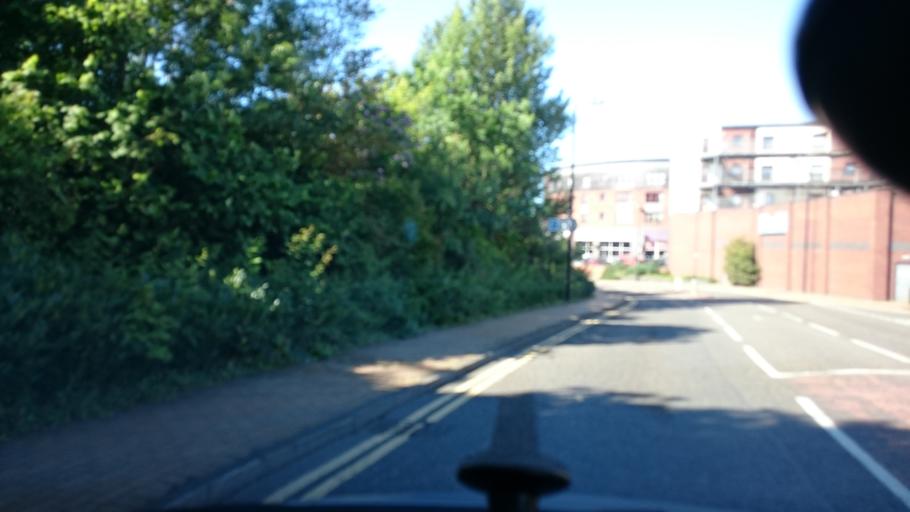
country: GB
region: Scotland
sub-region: Clackmannanshire
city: Alloa
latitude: 56.1154
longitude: -3.7881
